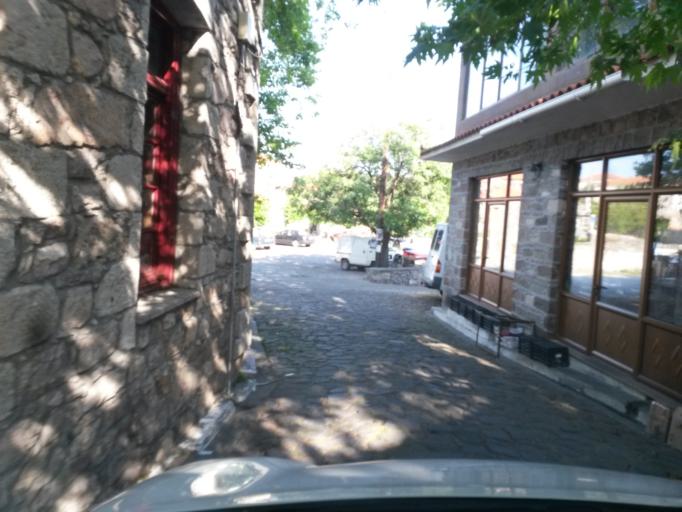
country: GR
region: North Aegean
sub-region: Nomos Lesvou
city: Mantamados
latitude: 39.3466
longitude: 26.3240
